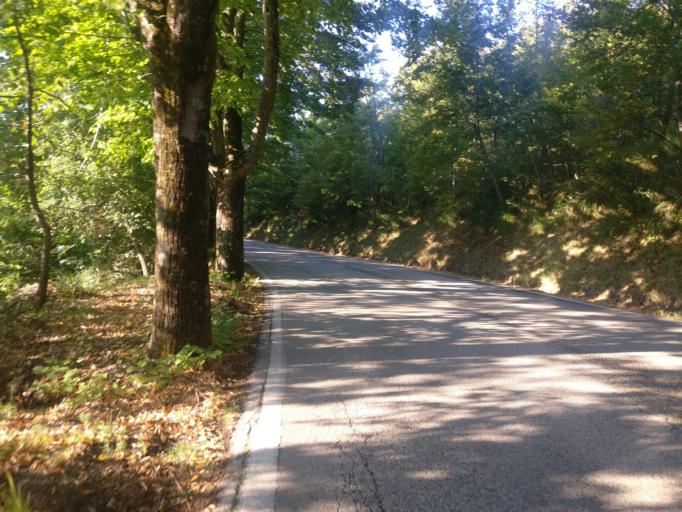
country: IT
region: The Marches
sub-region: Provincia di Ascoli Piceno
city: Montedinove
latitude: 42.9797
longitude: 13.5960
